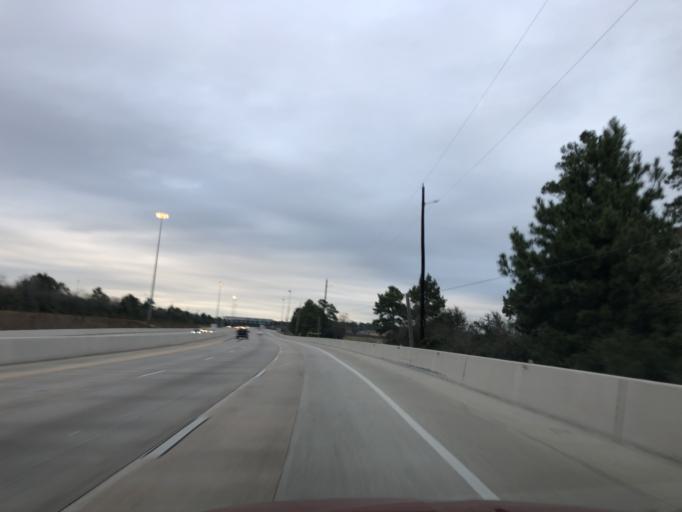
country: US
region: Texas
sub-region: Harris County
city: Spring
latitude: 30.0537
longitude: -95.4035
